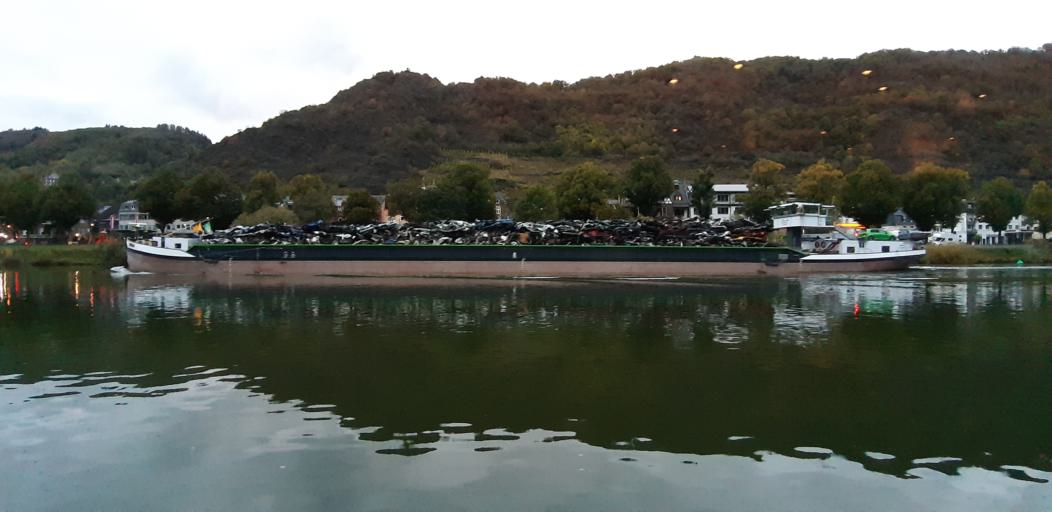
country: DE
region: Rheinland-Pfalz
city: Cochem
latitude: 50.1467
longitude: 7.1742
